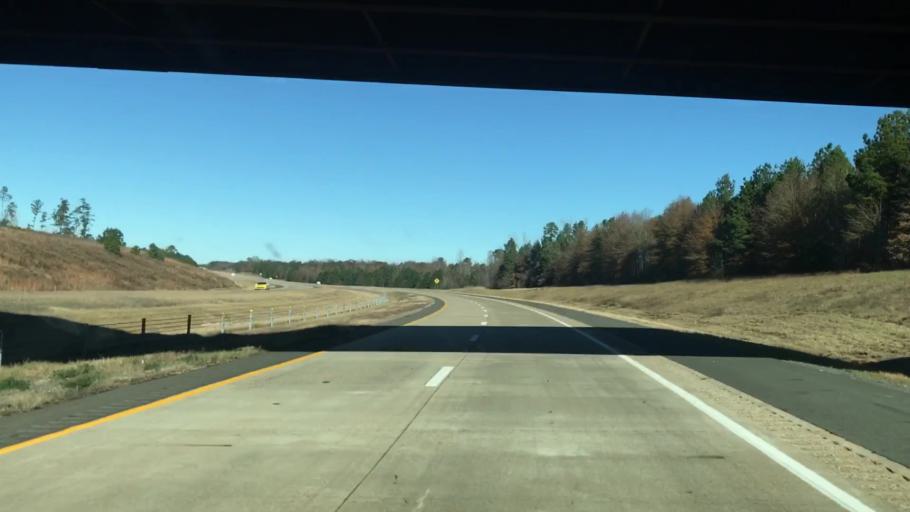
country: US
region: Texas
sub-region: Bowie County
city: Texarkana
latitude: 33.2693
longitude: -93.8980
